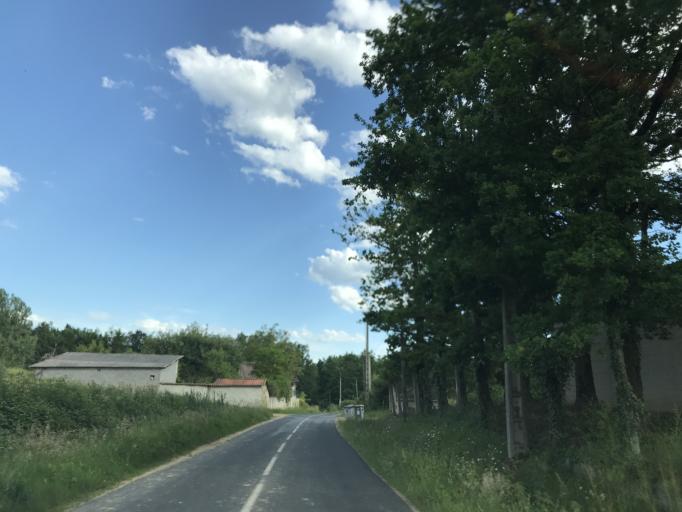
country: FR
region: Auvergne
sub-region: Departement du Puy-de-Dome
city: Courpiere
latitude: 45.7653
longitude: 3.6009
